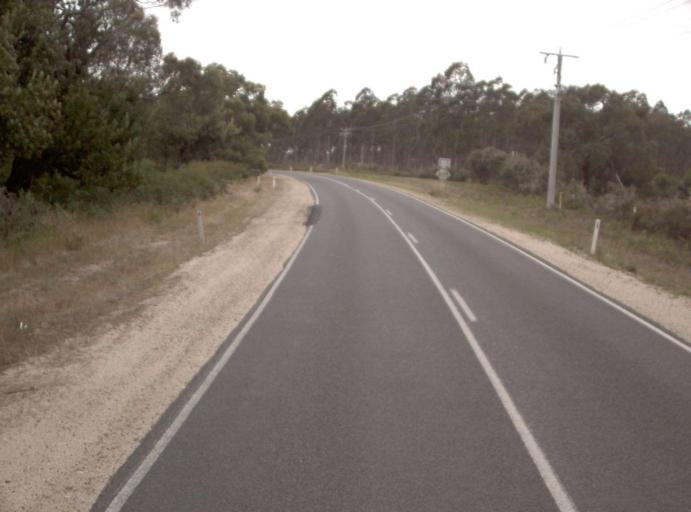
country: AU
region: Victoria
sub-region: Wellington
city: Sale
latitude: -38.1816
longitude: 147.1355
